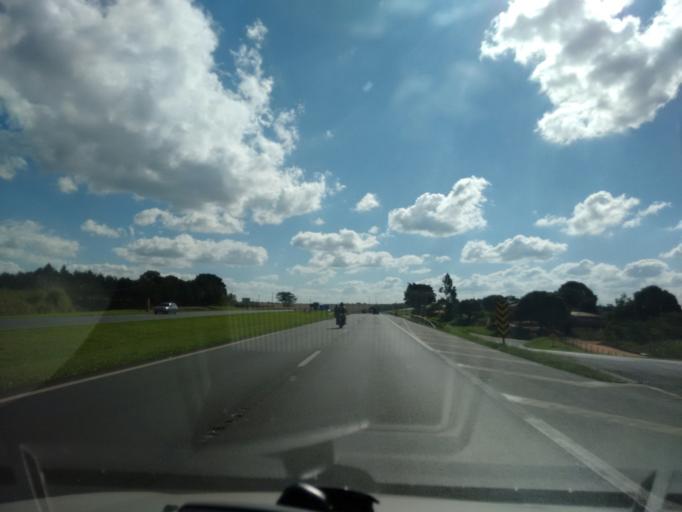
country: BR
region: Sao Paulo
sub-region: Ibate
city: Ibate
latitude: -21.9645
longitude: -47.9702
